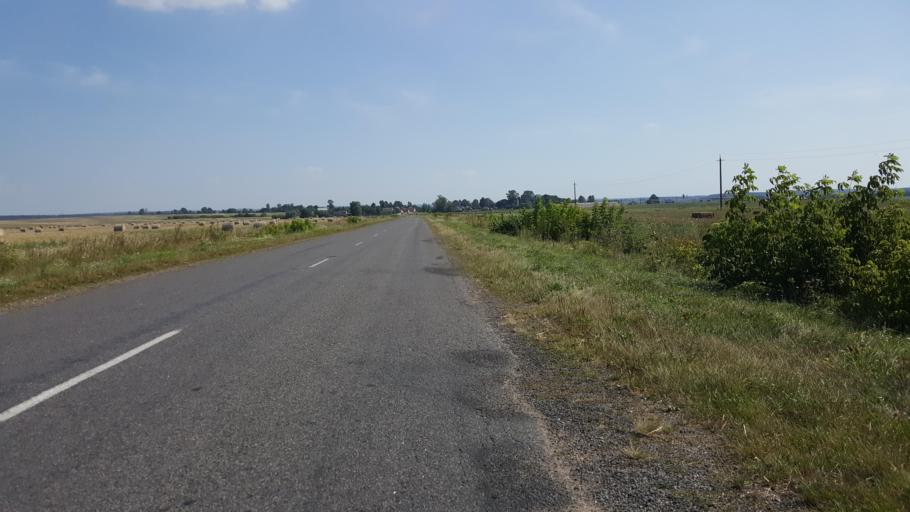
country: BY
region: Brest
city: Kamyanyets
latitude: 52.4389
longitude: 23.7444
